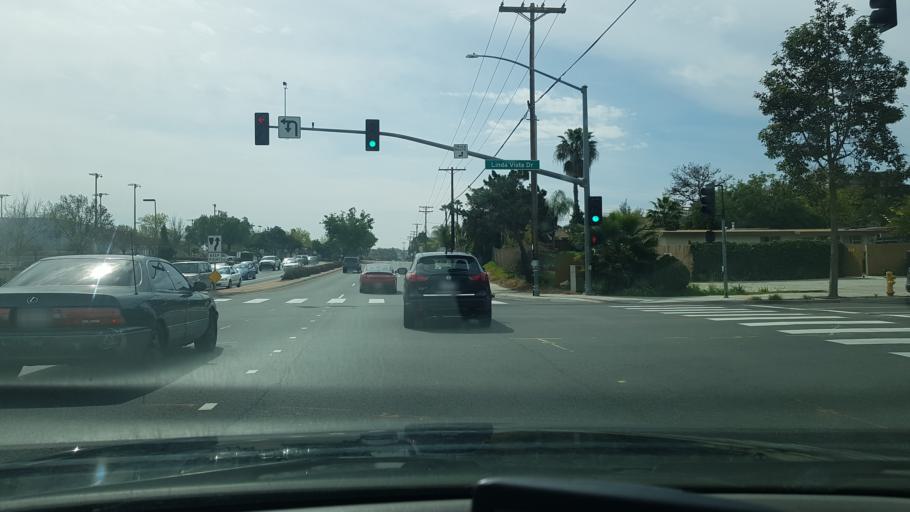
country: US
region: California
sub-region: San Diego County
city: Lake San Marcos
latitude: 33.1405
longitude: -117.2033
